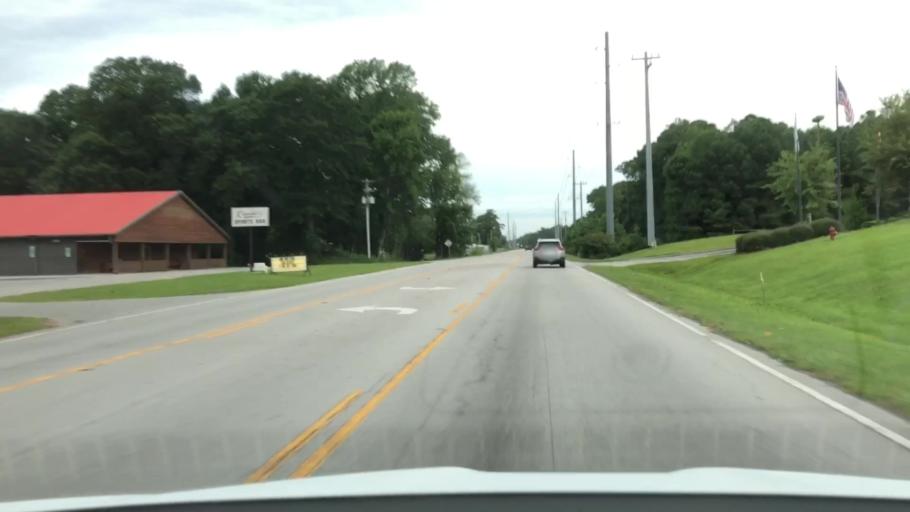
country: US
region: North Carolina
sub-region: Carteret County
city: Cape Carteret
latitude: 34.7172
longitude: -77.0695
